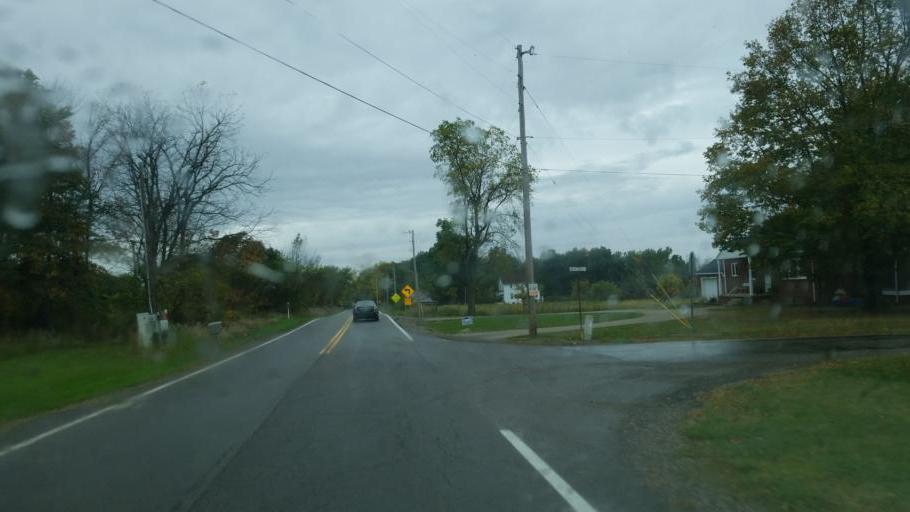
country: US
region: Ohio
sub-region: Richland County
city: Lincoln Heights
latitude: 40.8512
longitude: -82.4596
